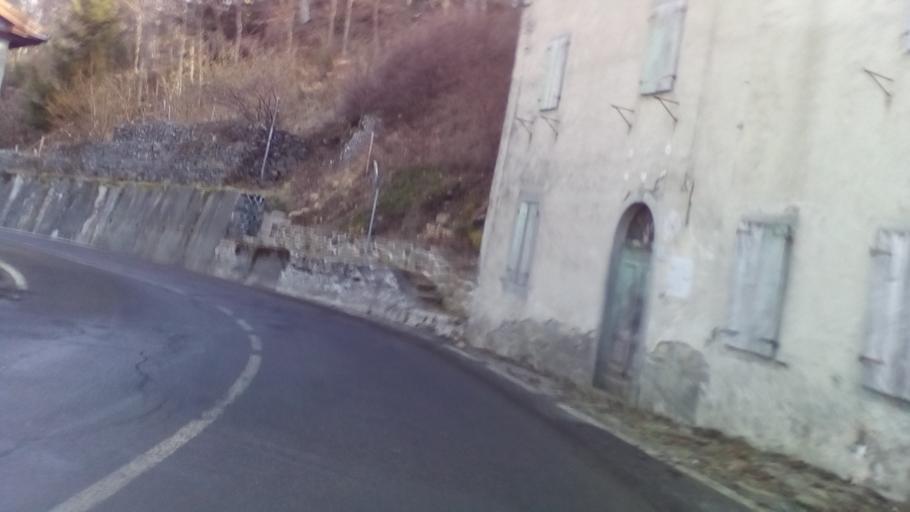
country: IT
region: Emilia-Romagna
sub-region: Provincia di Modena
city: Pievepelago
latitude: 44.1904
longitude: 10.5832
